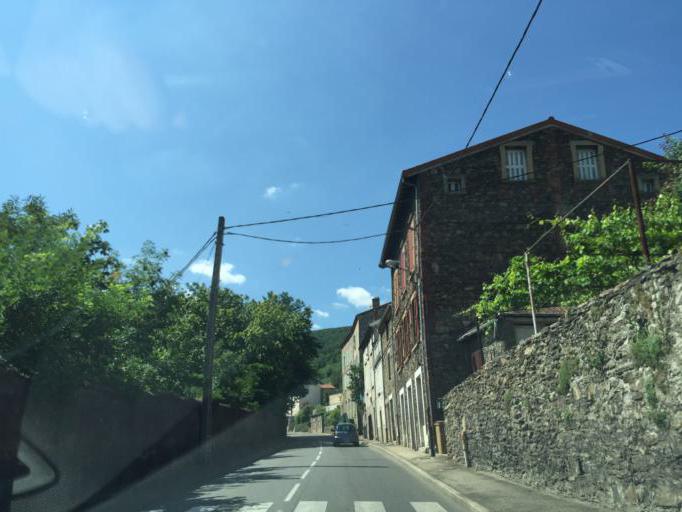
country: FR
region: Rhone-Alpes
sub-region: Departement de la Loire
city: Saint-Chamond
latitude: 45.4507
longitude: 4.5036
